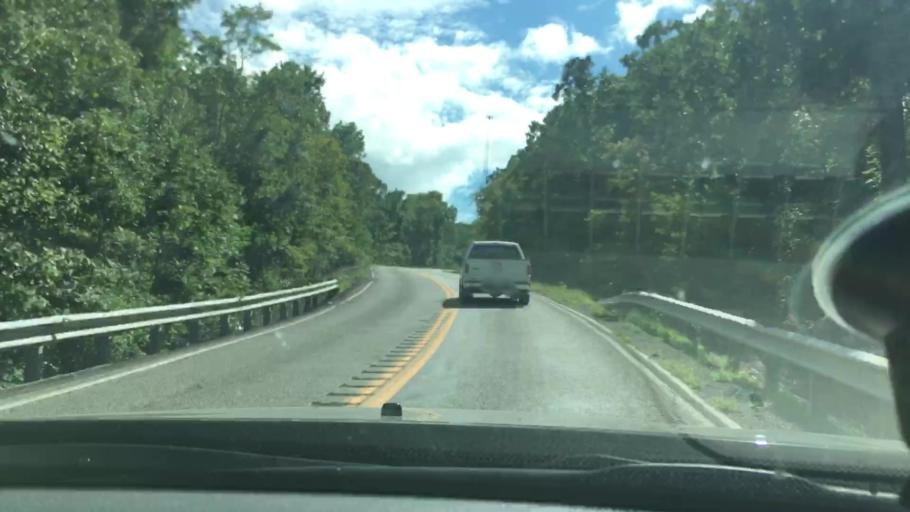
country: US
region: Oklahoma
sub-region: Sequoyah County
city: Vian
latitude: 35.6349
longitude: -94.9626
